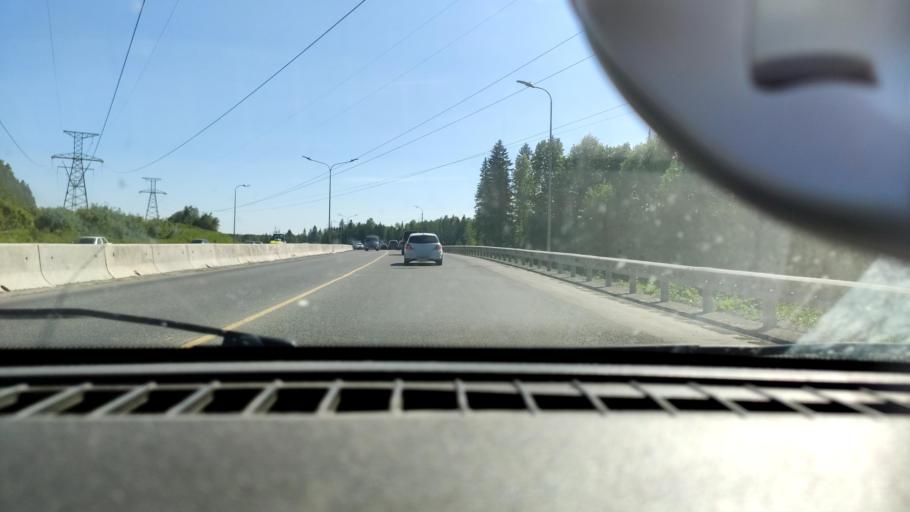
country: RU
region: Perm
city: Novyye Lyady
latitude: 58.0652
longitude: 56.4281
